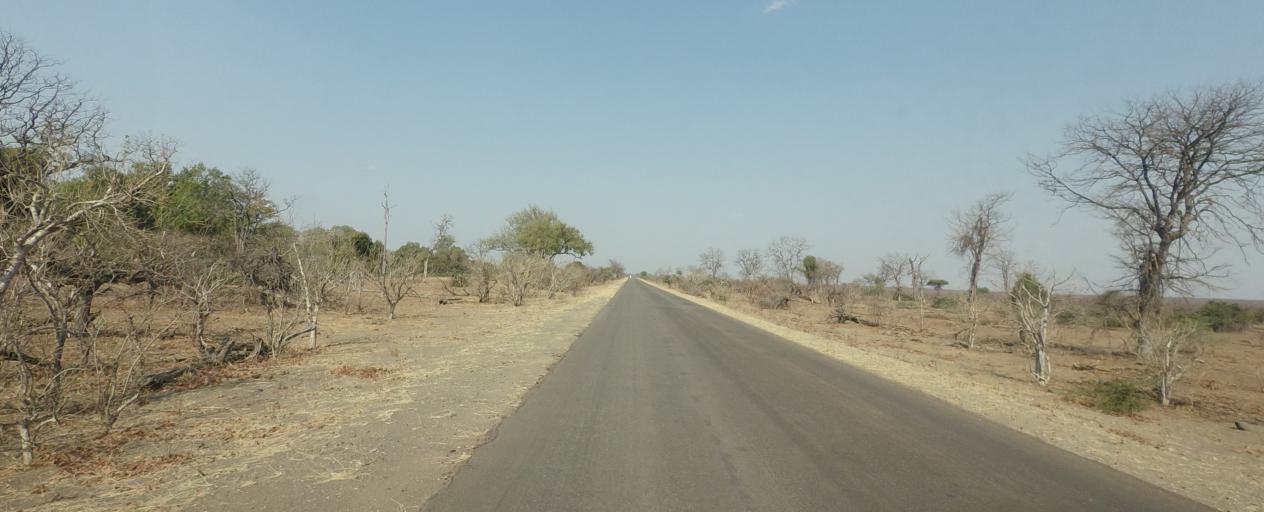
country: ZA
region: Limpopo
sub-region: Mopani District Municipality
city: Giyani
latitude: -23.0971
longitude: 31.3980
